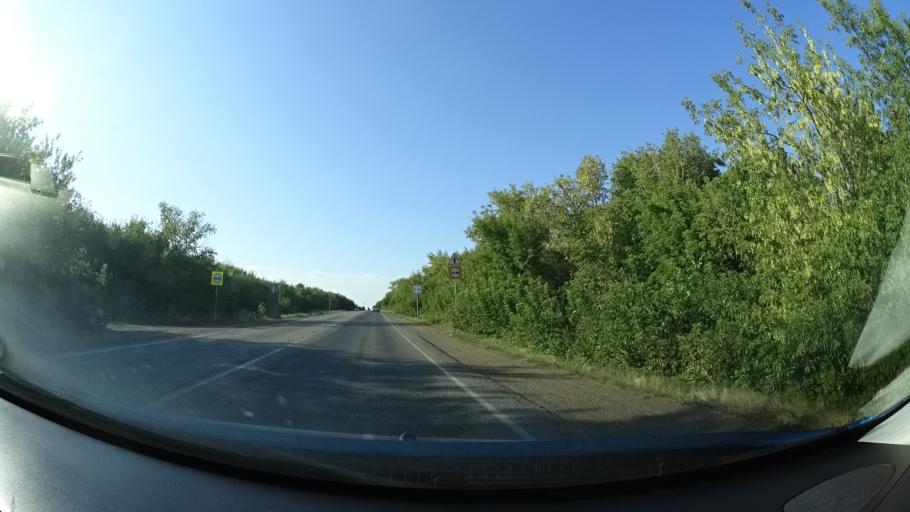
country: RU
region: Bashkortostan
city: Salavat
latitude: 53.4486
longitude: 55.9217
